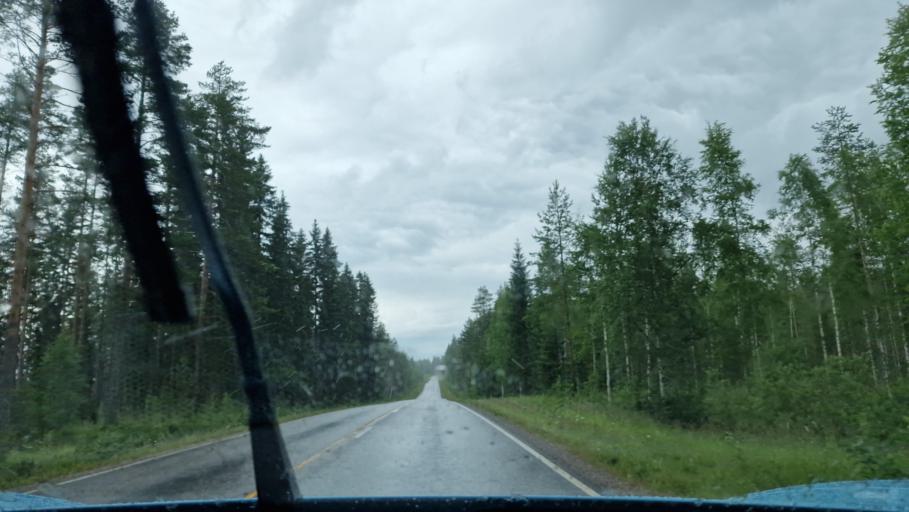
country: FI
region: Central Finland
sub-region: Saarijaervi-Viitasaari
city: Pylkoenmaeki
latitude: 62.5938
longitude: 24.5904
